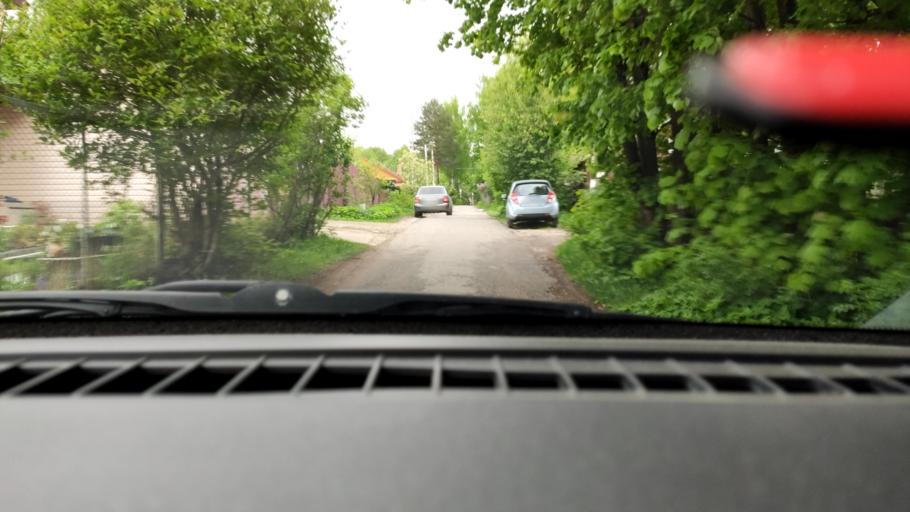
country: RU
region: Perm
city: Kondratovo
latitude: 58.0574
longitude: 56.1328
